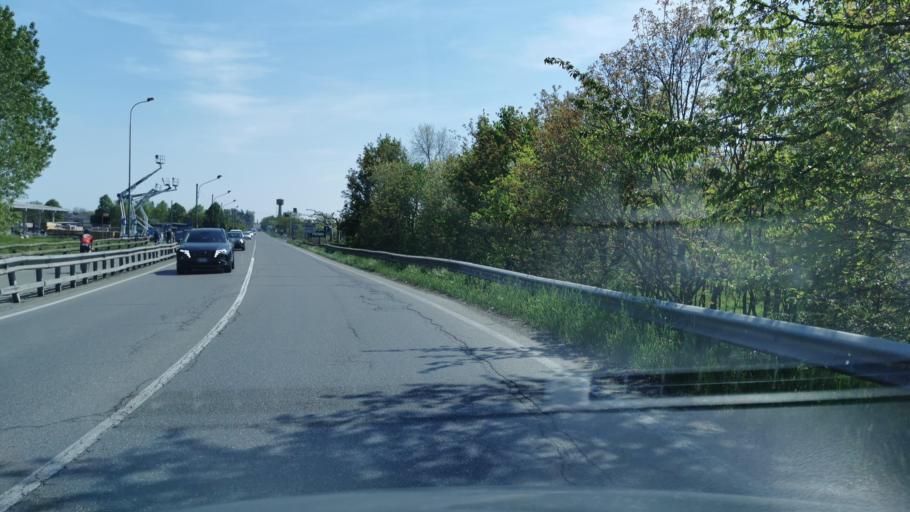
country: IT
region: Emilia-Romagna
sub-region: Provincia di Piacenza
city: Castelvetro Piacentino
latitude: 45.1214
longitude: 9.9881
